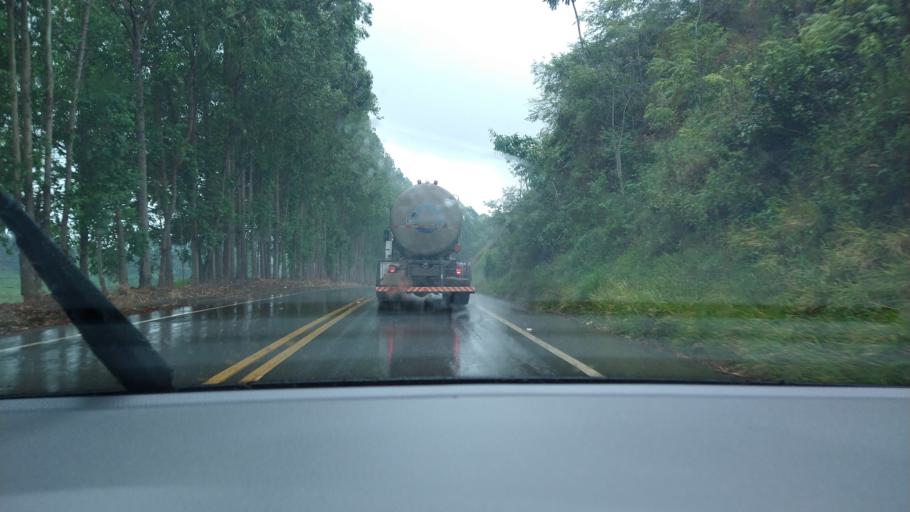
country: BR
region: Minas Gerais
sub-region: Vicosa
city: Vicosa
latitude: -20.5936
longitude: -42.8806
